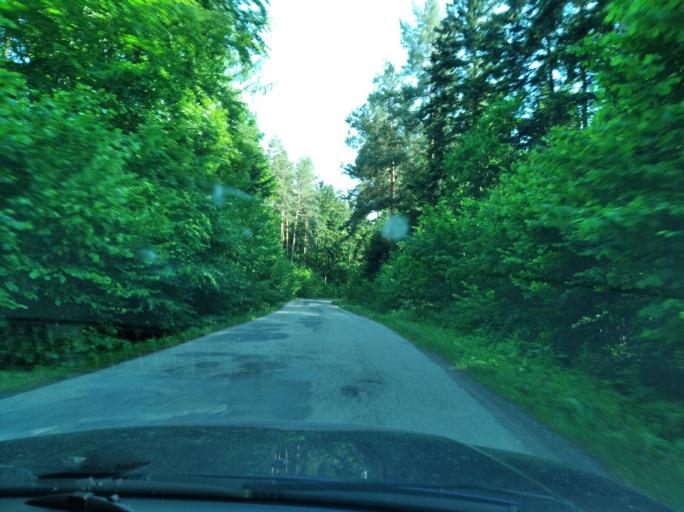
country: PL
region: Subcarpathian Voivodeship
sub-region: Powiat jaroslawski
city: Kramarzowka
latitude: 49.8557
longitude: 22.5162
